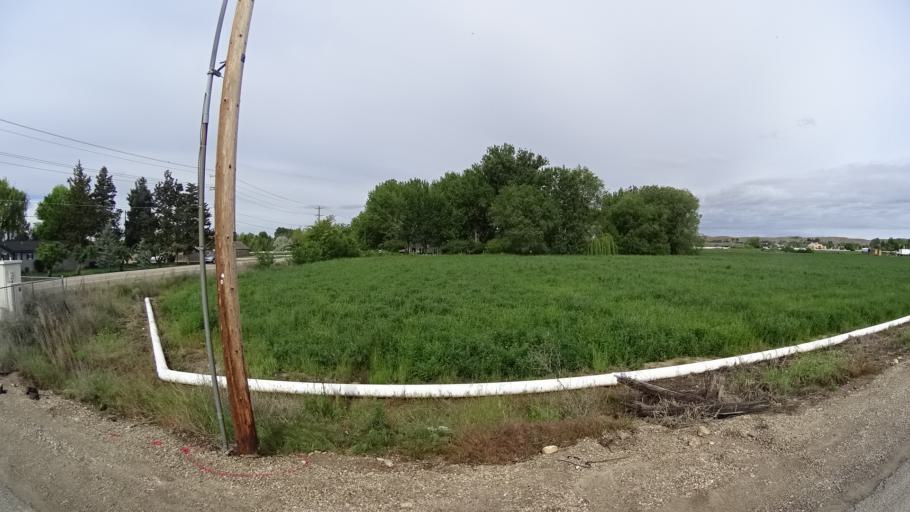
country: US
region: Idaho
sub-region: Ada County
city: Eagle
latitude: 43.7212
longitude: -116.4034
